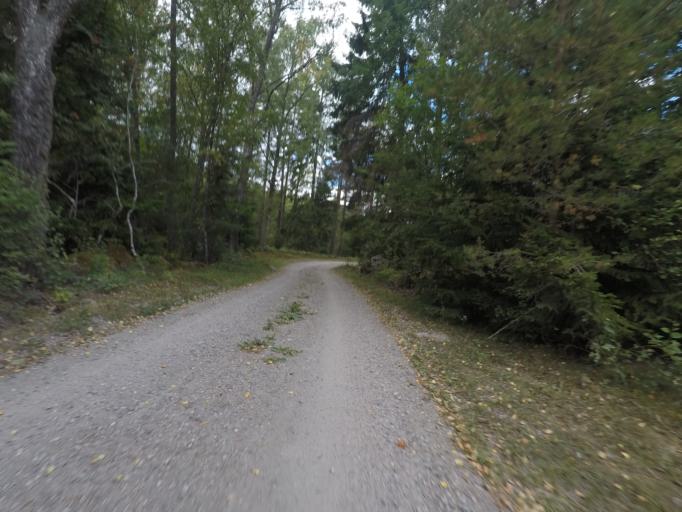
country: SE
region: Soedermanland
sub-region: Eskilstuna Kommun
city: Kvicksund
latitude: 59.4238
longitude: 16.2851
